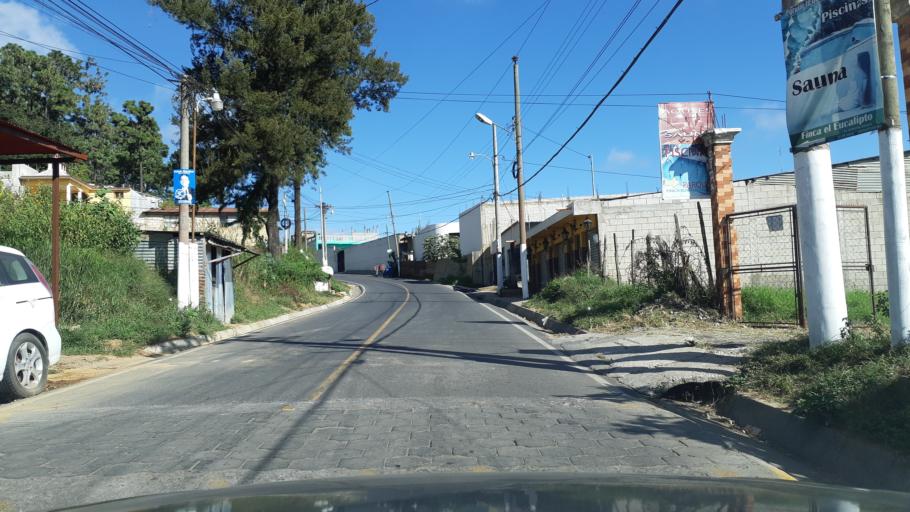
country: GT
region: Chimaltenango
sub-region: Municipio de Chimaltenango
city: Chimaltenango
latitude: 14.6523
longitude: -90.8202
